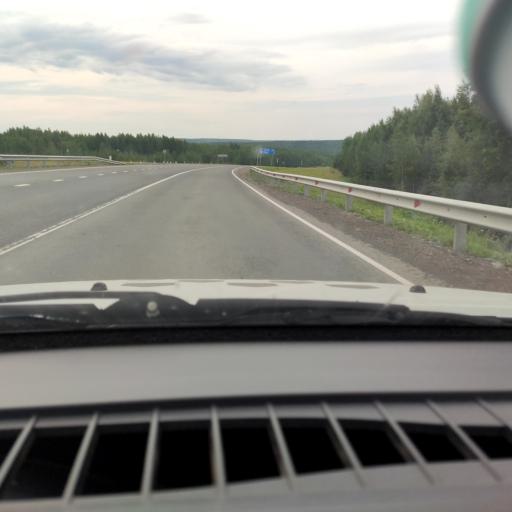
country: RU
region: Kirov
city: Kostino
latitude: 58.8115
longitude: 53.5942
